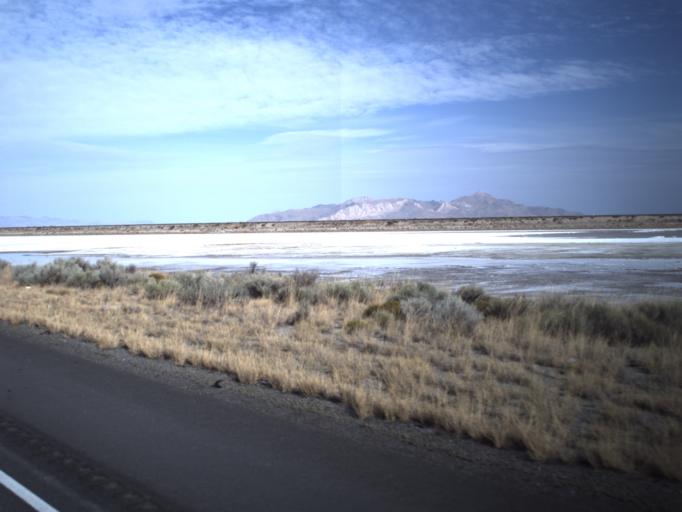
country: US
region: Utah
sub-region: Tooele County
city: Stansbury park
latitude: 40.6648
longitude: -112.3624
